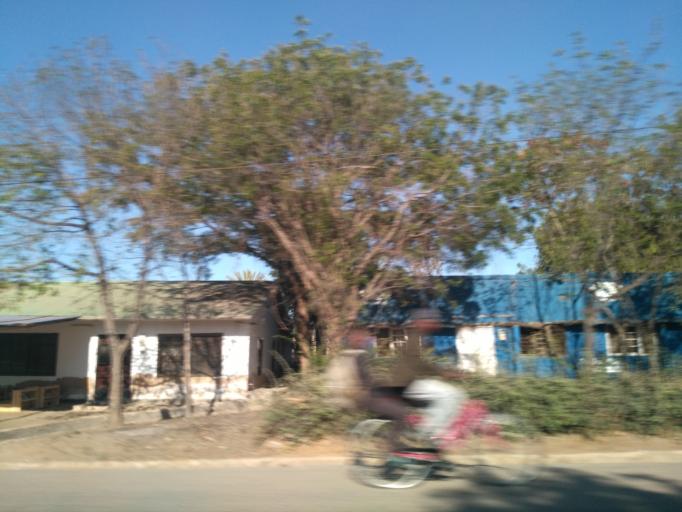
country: TZ
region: Dodoma
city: Dodoma
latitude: -6.1512
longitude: 35.7476
